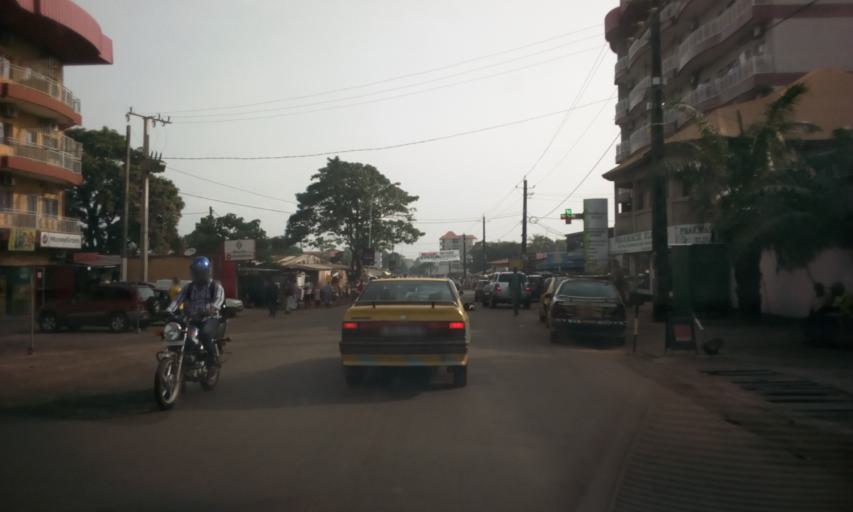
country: GN
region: Conakry
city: Conakry
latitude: 9.6106
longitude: -13.6461
